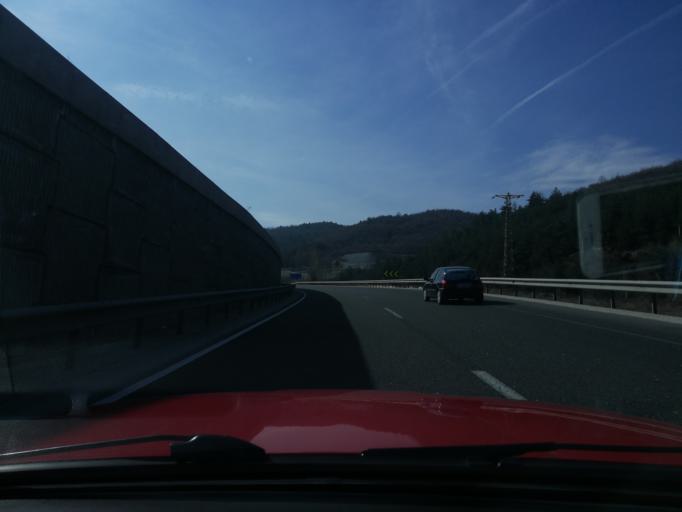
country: TR
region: Bilecik
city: Kuplu
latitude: 40.0392
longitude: 30.0201
